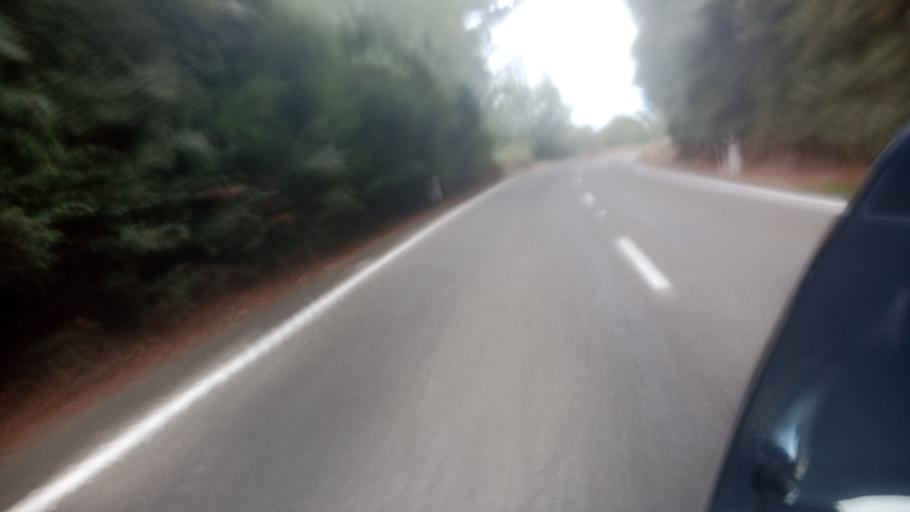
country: NZ
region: Bay of Plenty
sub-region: Opotiki District
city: Opotiki
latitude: -38.4068
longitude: 177.5615
